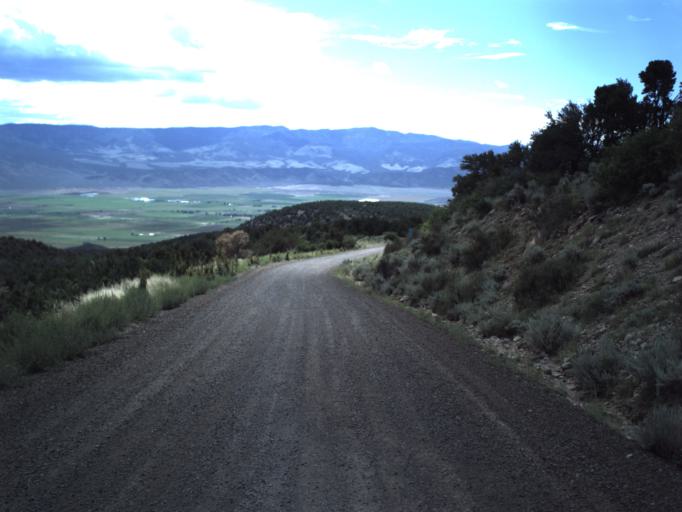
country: US
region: Utah
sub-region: Piute County
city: Junction
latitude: 38.2526
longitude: -112.3137
